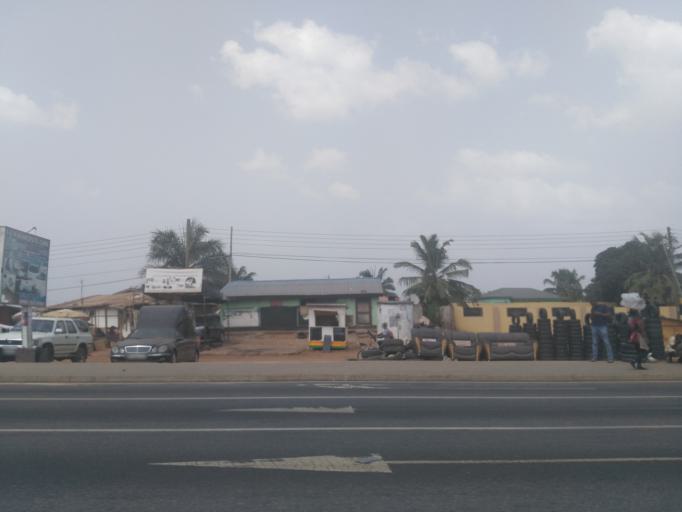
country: GH
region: Greater Accra
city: Gbawe
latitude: 5.5927
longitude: -0.2677
